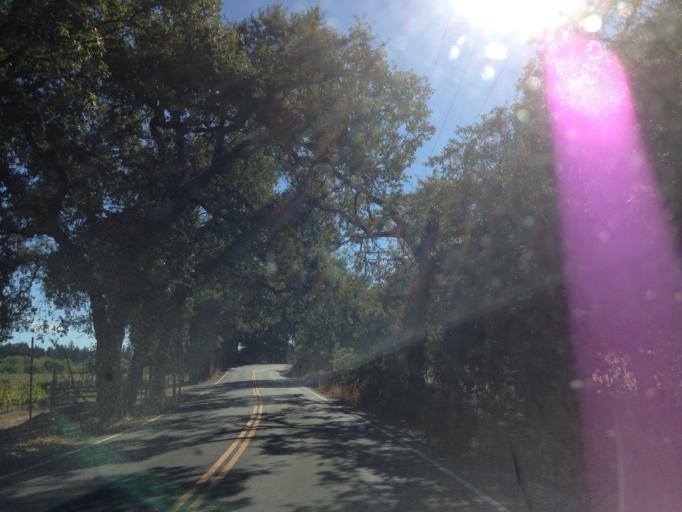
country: US
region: California
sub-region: Sonoma County
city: Forestville
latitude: 38.5048
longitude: -122.8876
